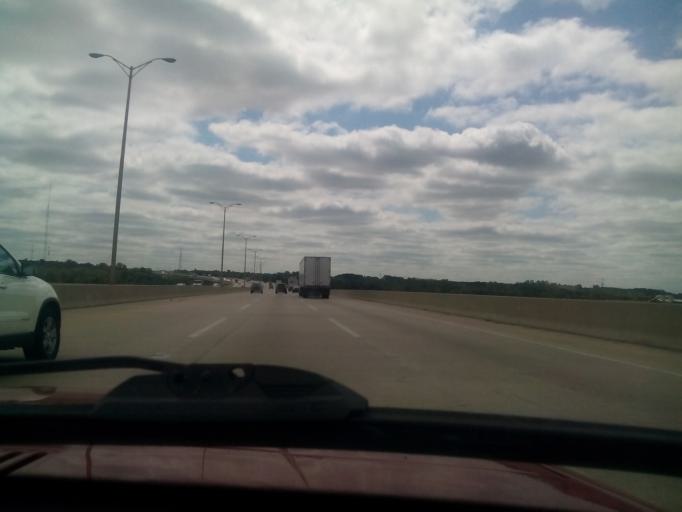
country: US
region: Illinois
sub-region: Cook County
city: Lemont
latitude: 41.6735
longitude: -88.0296
